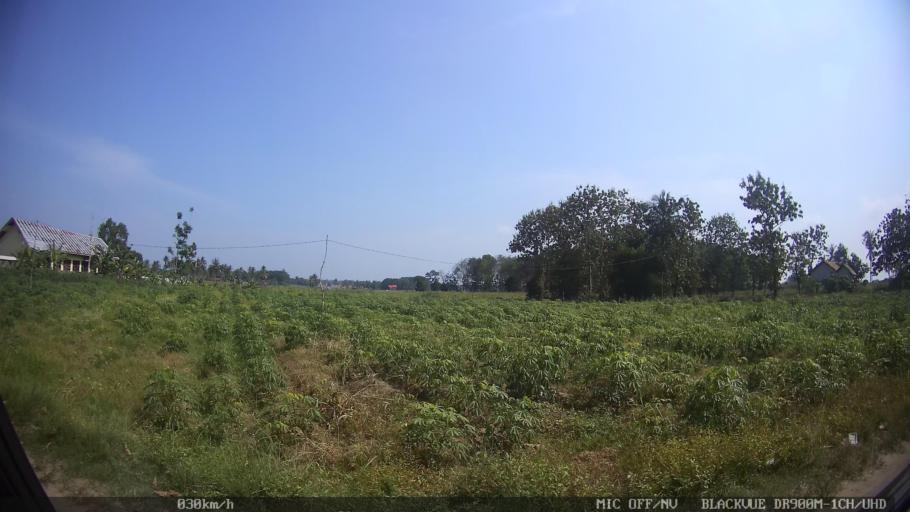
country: ID
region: Lampung
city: Natar
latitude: -5.2538
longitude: 105.2008
